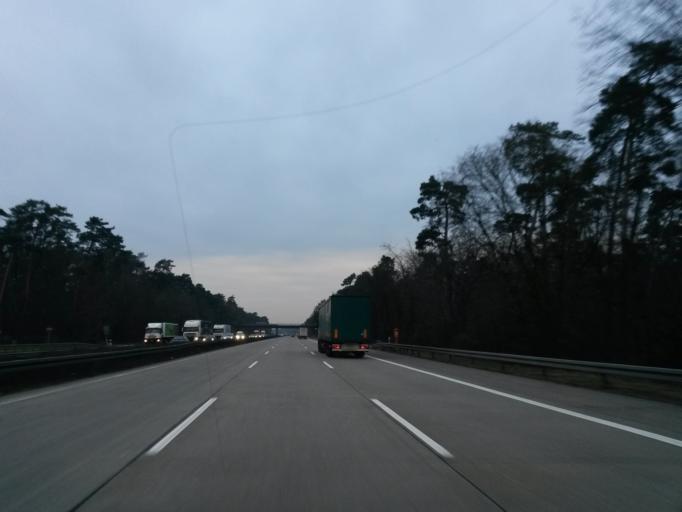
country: DE
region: Baden-Wuerttemberg
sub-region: Karlsruhe Region
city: Reilingen
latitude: 49.2985
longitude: 8.5943
